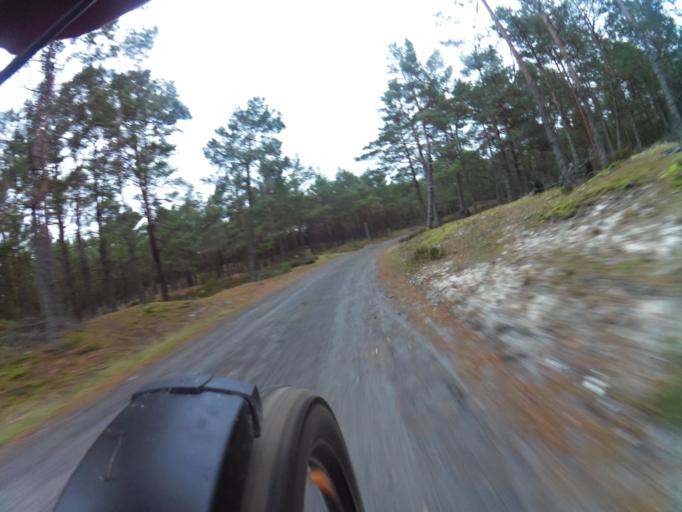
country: PL
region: Pomeranian Voivodeship
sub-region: Powiat wejherowski
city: Choczewo
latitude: 54.7874
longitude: 17.7472
